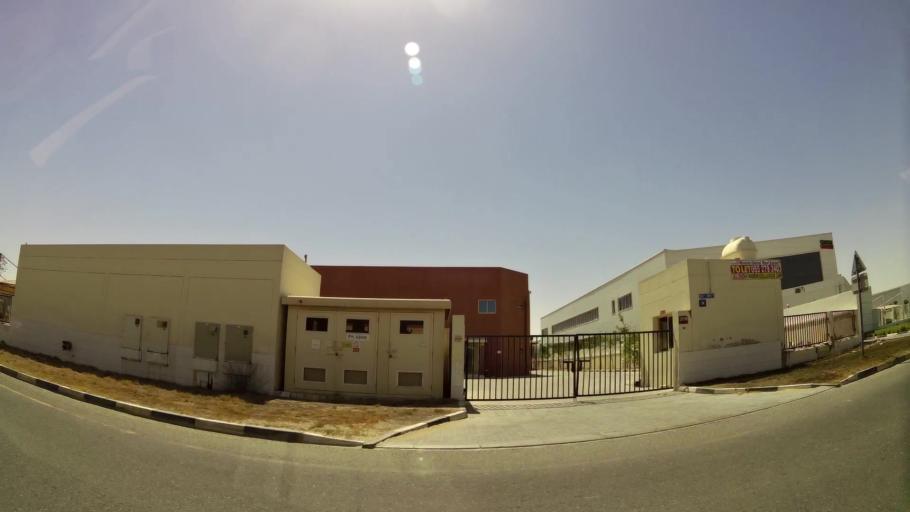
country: AE
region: Dubai
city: Dubai
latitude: 24.9706
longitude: 55.2011
